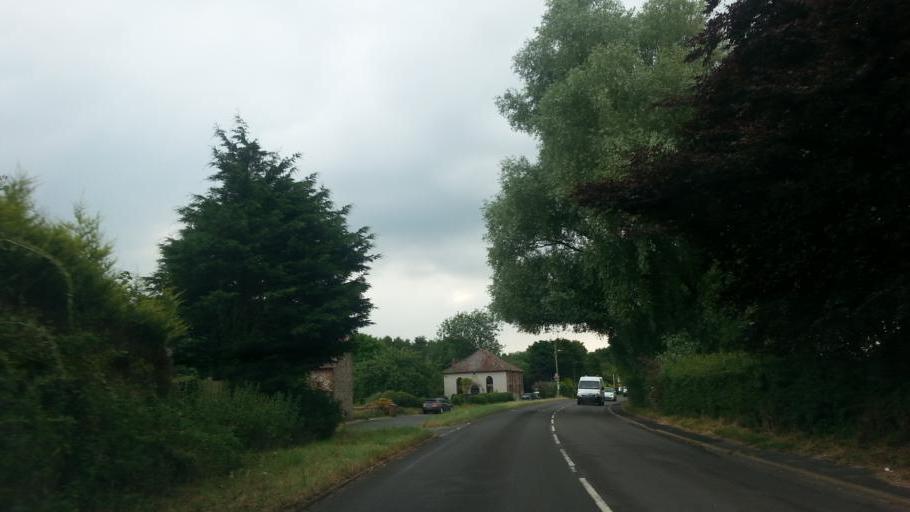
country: GB
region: England
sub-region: Norfolk
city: Fakenham
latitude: 52.8193
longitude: 0.7072
